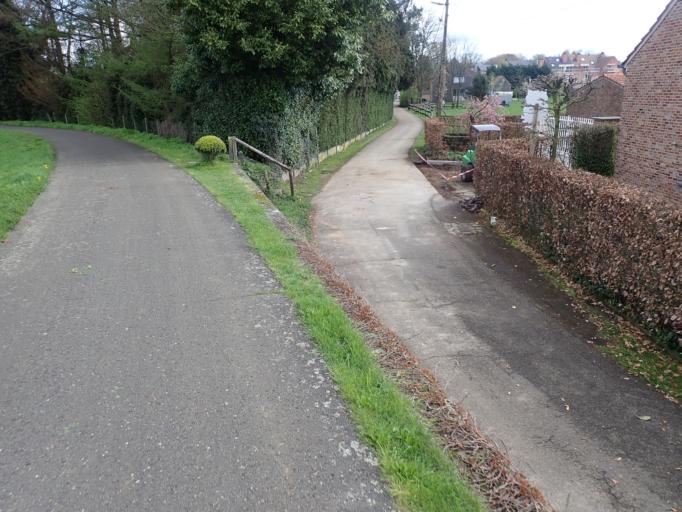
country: BE
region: Flanders
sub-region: Provincie Antwerpen
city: Grobbendonk
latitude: 51.1872
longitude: 4.7365
